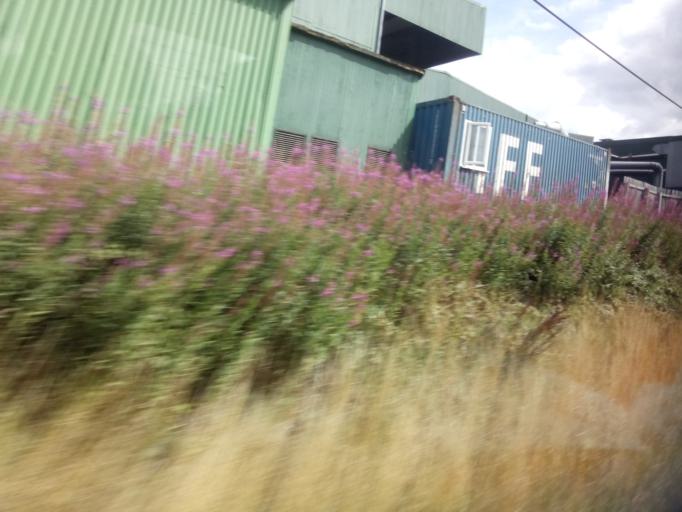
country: GB
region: England
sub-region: Gateshead
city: Lamesley
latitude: 54.9173
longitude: -1.6016
